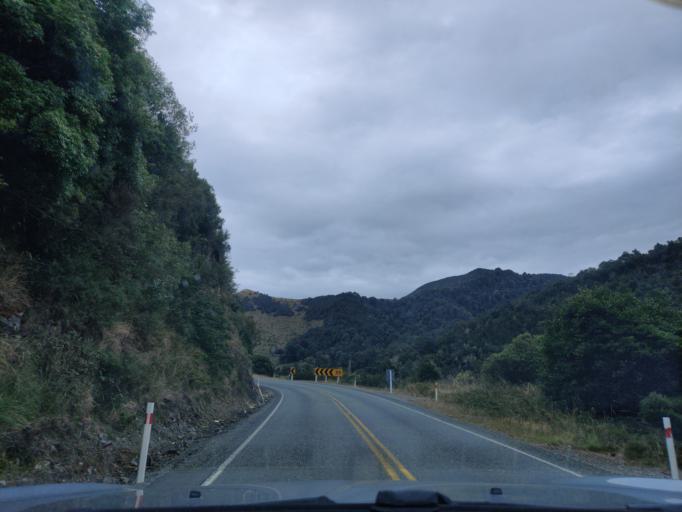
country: NZ
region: Tasman
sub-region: Tasman District
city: Wakefield
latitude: -41.6986
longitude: 172.6228
